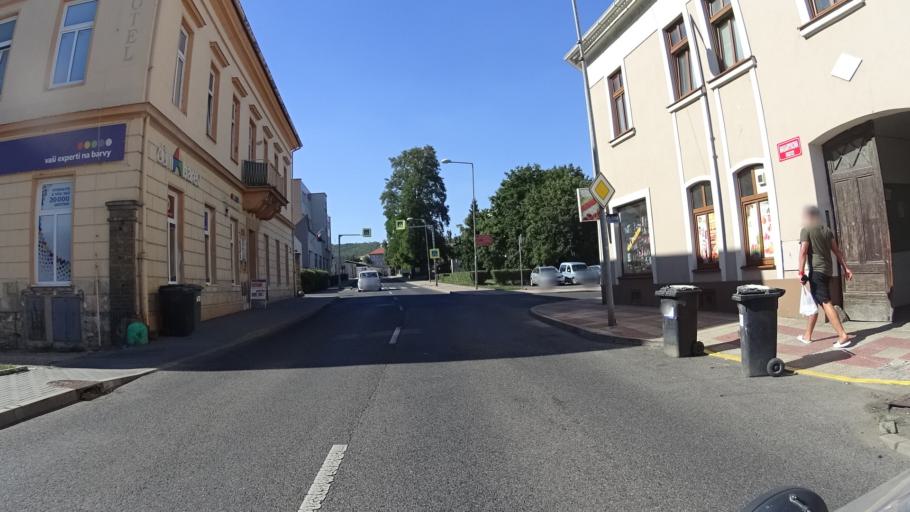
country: CZ
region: Ustecky
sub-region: Okres Litomerice
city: Litomerice
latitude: 50.5385
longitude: 14.1273
